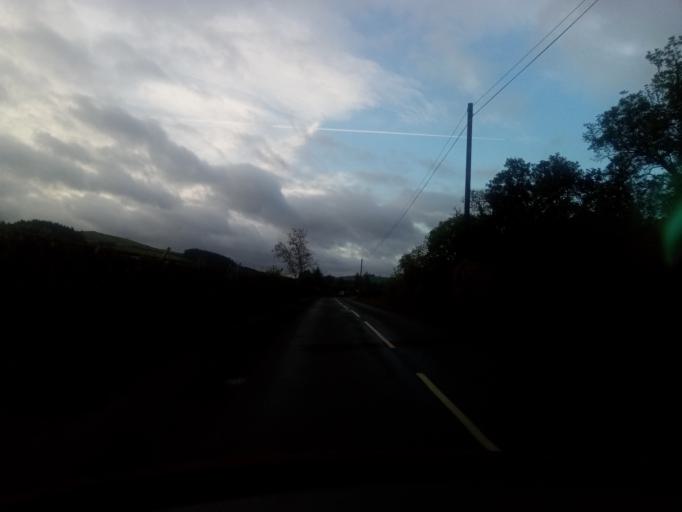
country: GB
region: Scotland
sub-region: The Scottish Borders
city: Jedburgh
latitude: 55.4156
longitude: -2.6370
